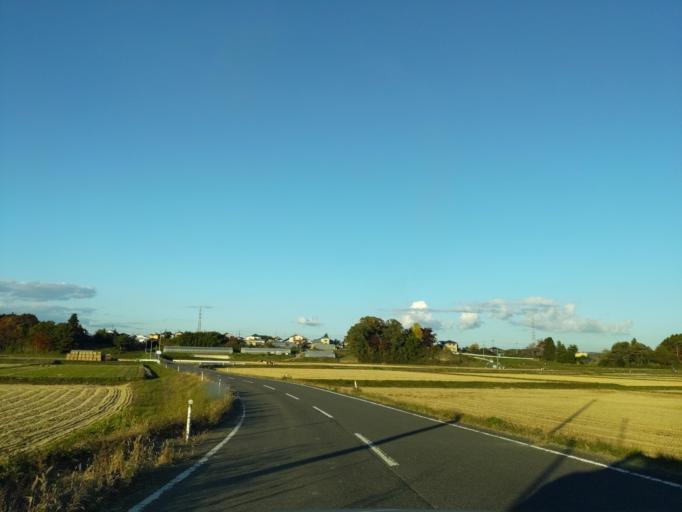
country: JP
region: Fukushima
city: Koriyama
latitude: 37.4514
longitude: 140.3622
